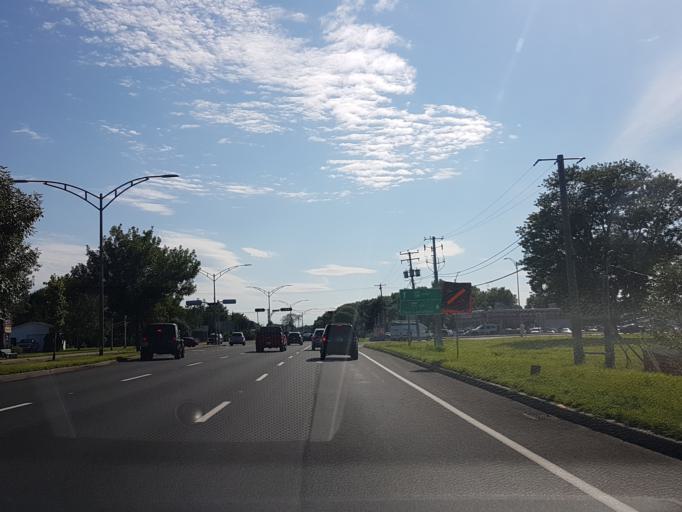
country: CA
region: Quebec
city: Sainte-Catherine
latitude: 46.3142
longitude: -72.5740
